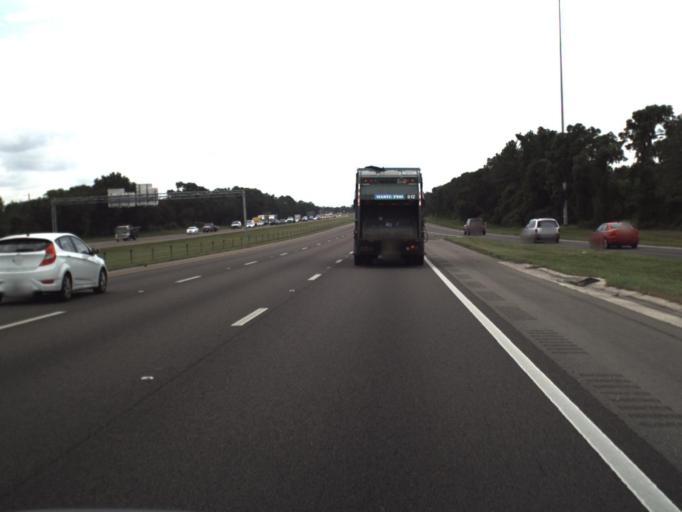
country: US
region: Florida
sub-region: Sarasota County
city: Desoto Lakes
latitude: 27.4377
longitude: -82.4597
